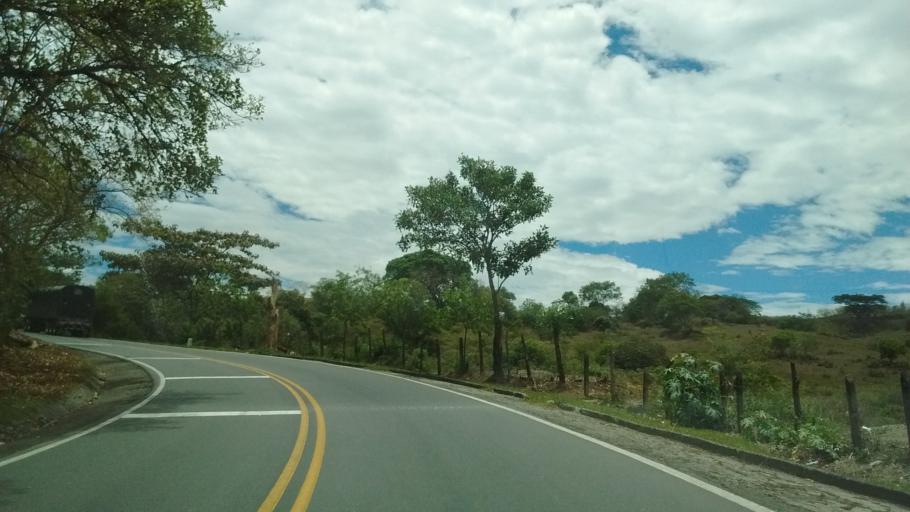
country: CO
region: Cauca
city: La Sierra
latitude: 2.2157
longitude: -76.7968
